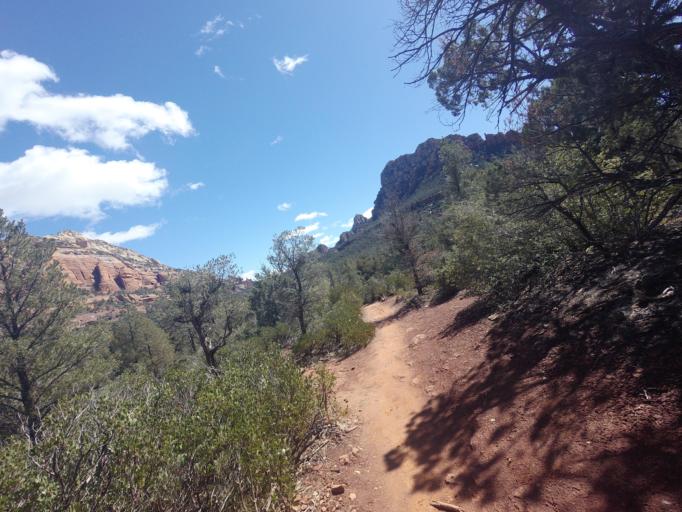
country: US
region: Arizona
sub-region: Yavapai County
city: West Sedona
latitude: 34.9035
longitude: -111.8159
